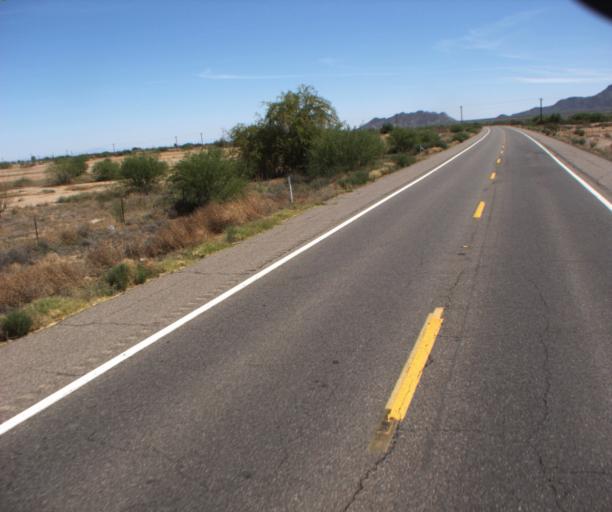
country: US
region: Arizona
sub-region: Pinal County
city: Sacaton
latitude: 33.0760
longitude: -111.7025
